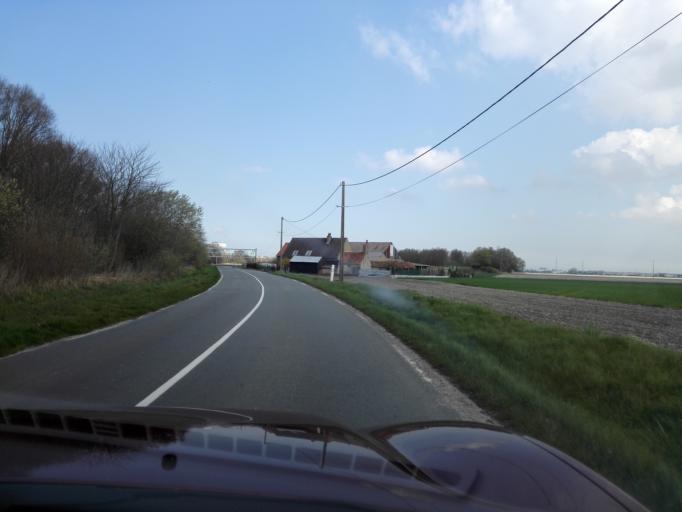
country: FR
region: Nord-Pas-de-Calais
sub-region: Departement du Nord
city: Brouckerque
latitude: 50.9718
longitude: 2.2831
